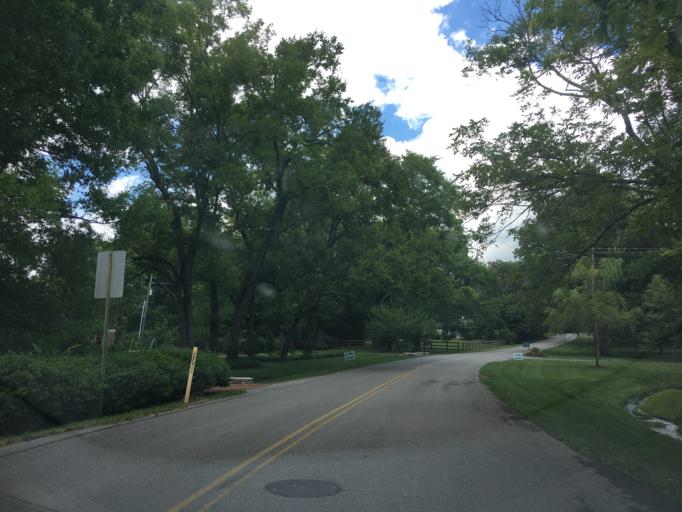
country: US
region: Tennessee
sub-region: Davidson County
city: Forest Hills
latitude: 36.0816
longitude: -86.8494
